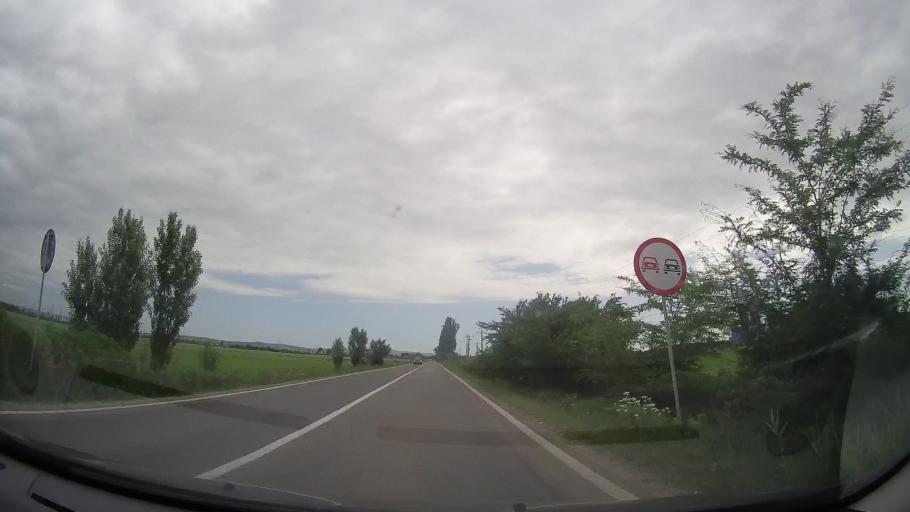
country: RO
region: Prahova
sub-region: Comuna Berceni
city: Corlatesti
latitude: 44.9065
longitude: 26.0748
